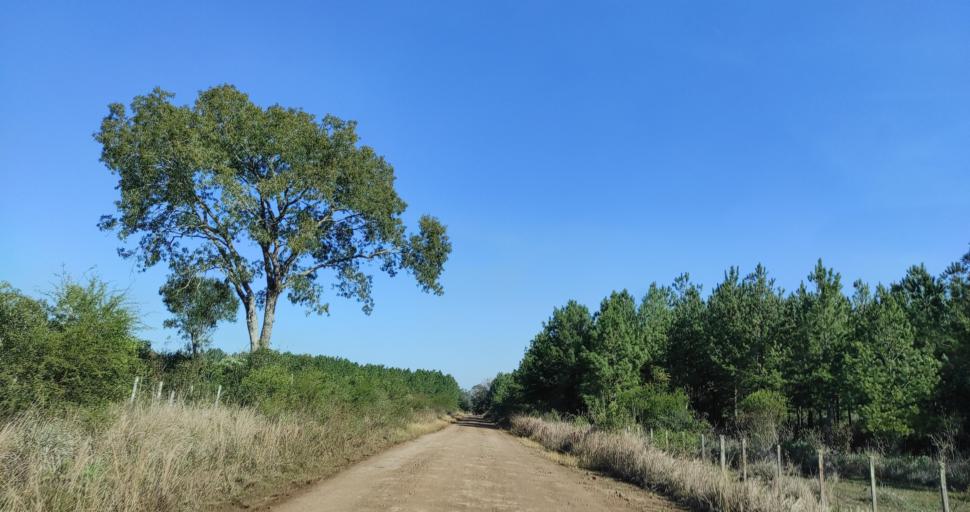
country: AR
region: Misiones
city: Cerro Cora
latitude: -27.6497
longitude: -55.6576
